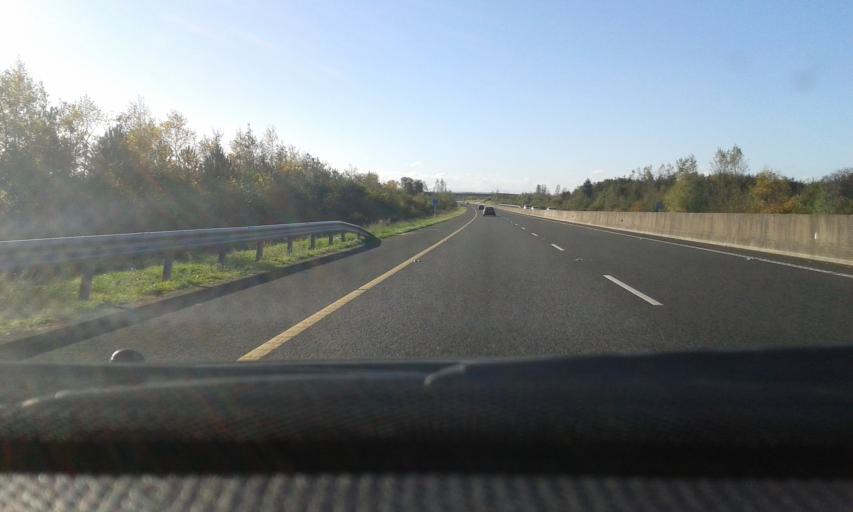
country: IE
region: Munster
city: Thurles
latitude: 52.6886
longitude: -7.6692
